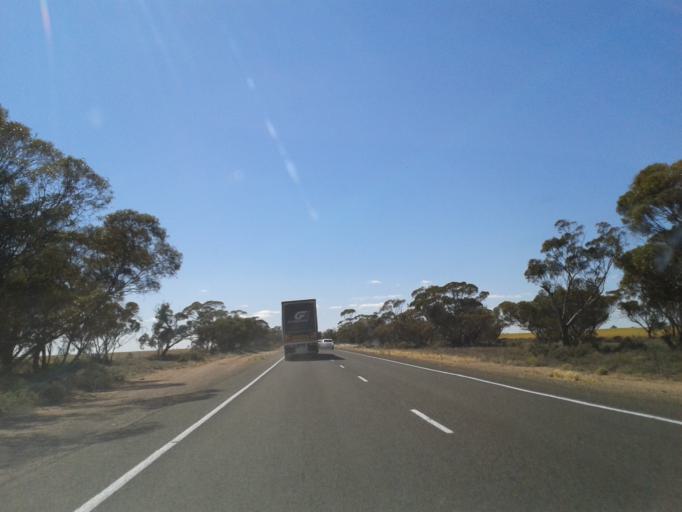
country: AU
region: New South Wales
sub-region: Wentworth
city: Dareton
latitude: -34.2766
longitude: 141.6976
